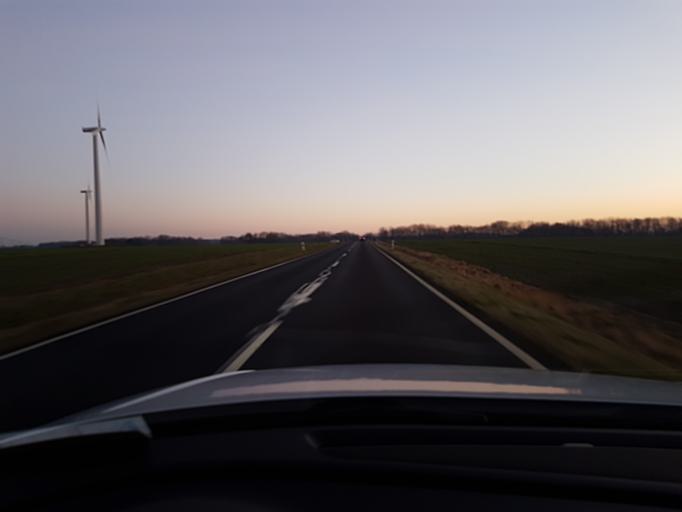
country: DE
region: Mecklenburg-Vorpommern
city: Gingst
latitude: 54.4795
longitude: 13.2910
